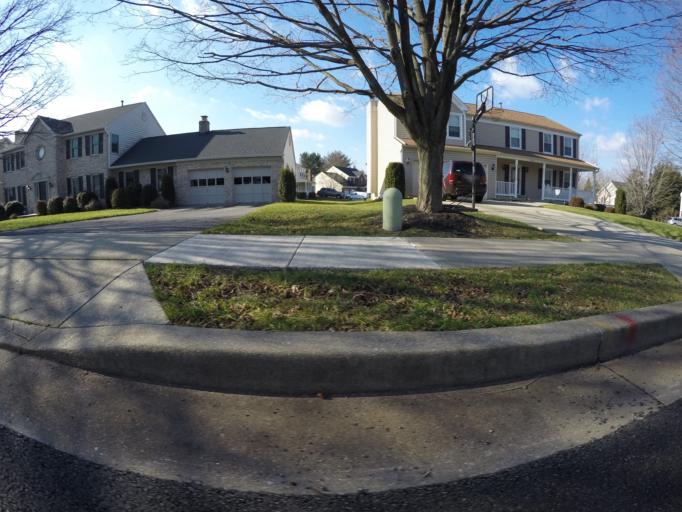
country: US
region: Maryland
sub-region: Howard County
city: Ilchester
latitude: 39.2202
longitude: -76.7928
